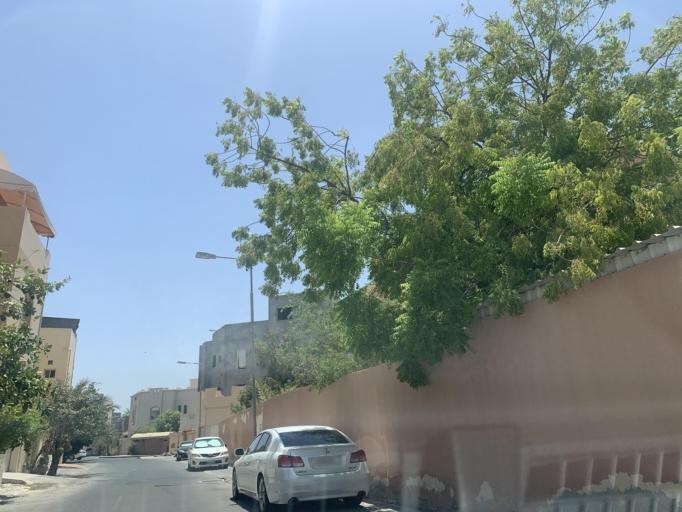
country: BH
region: Manama
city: Jidd Hafs
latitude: 26.2205
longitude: 50.5141
